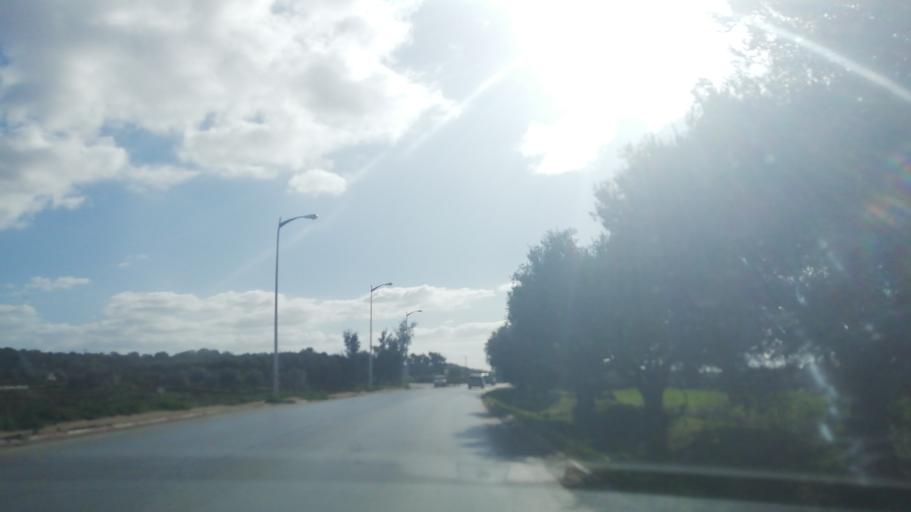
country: DZ
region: Mostaganem
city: Mostaganem
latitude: 35.9891
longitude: 0.2915
